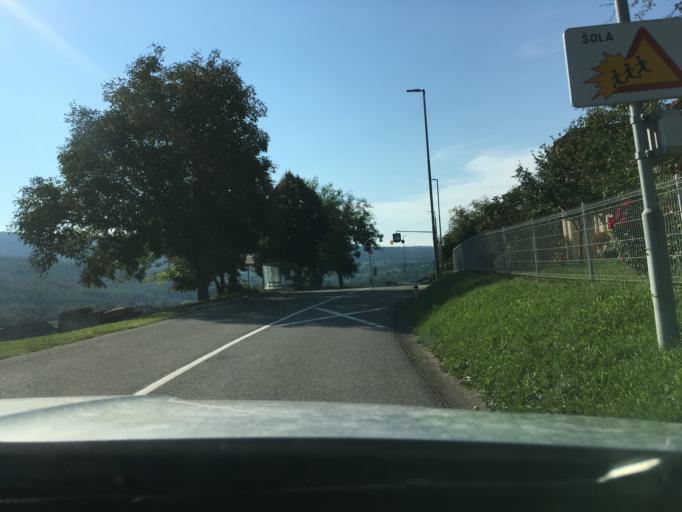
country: SI
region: Crnomelj
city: Crnomelj
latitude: 45.5190
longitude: 15.1763
